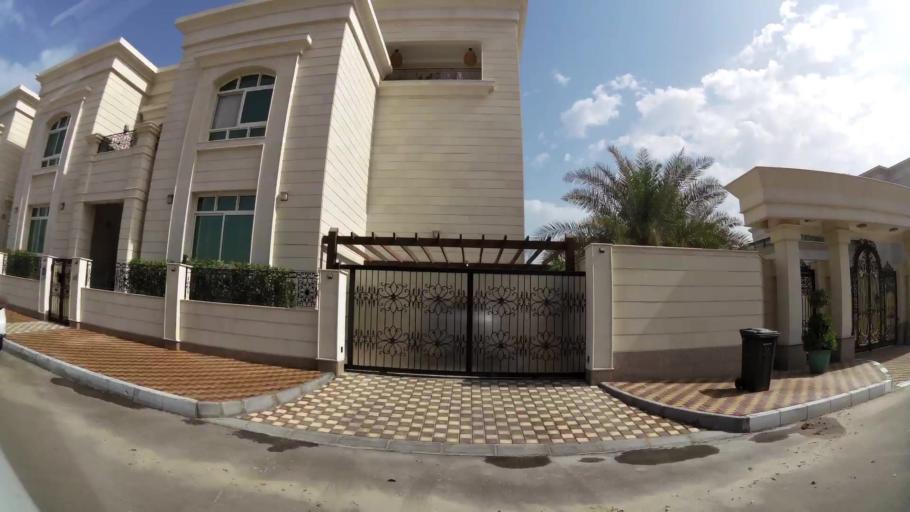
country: AE
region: Abu Dhabi
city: Abu Dhabi
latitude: 24.4443
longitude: 54.3593
